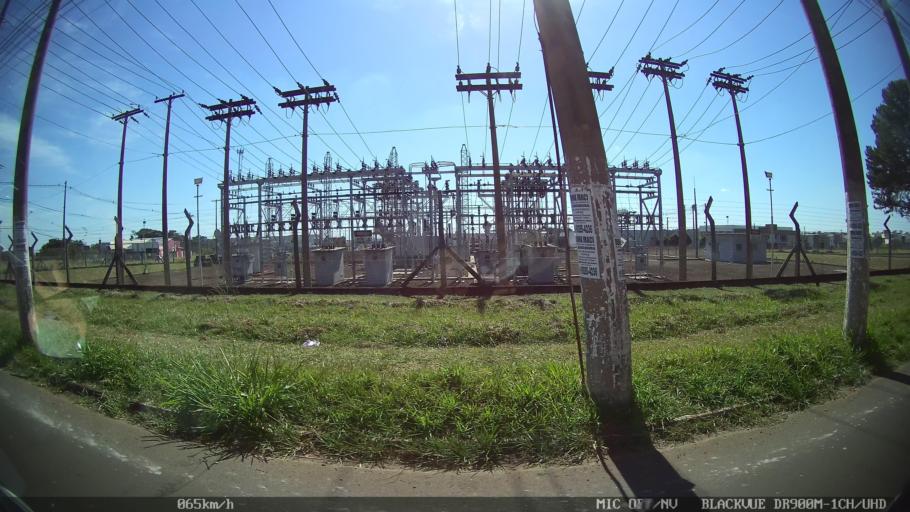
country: BR
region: Sao Paulo
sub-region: Franca
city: Franca
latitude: -20.5468
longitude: -47.4336
